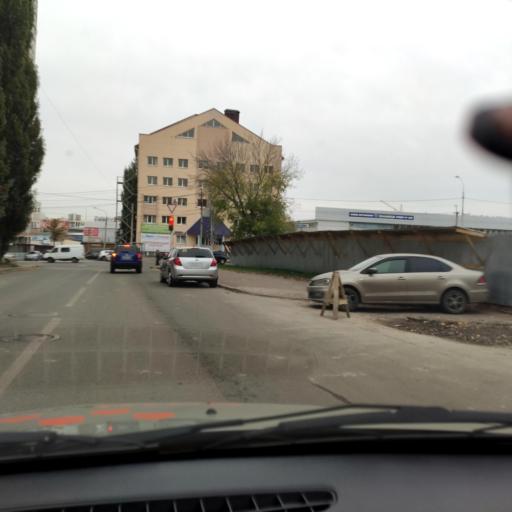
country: RU
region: Bashkortostan
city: Ufa
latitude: 54.7265
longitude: 55.9820
